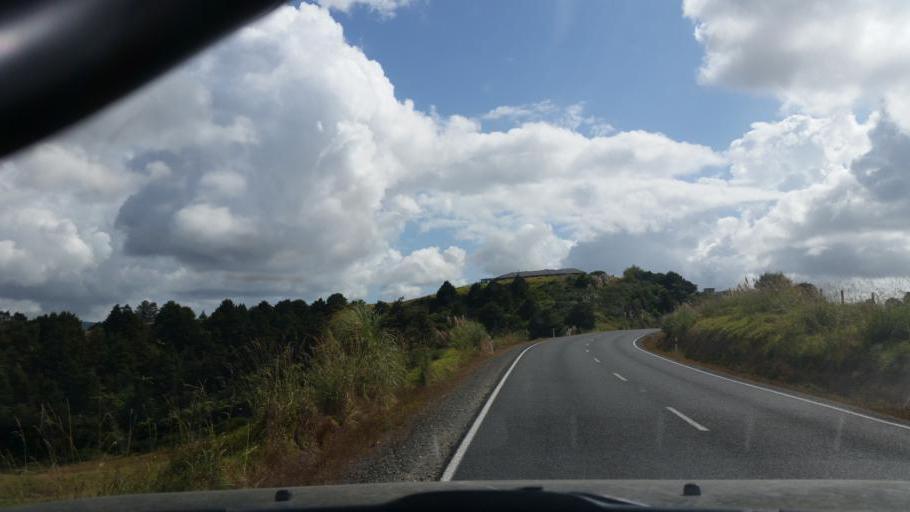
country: NZ
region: Auckland
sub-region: Auckland
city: Wellsford
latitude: -36.1347
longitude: 174.5271
